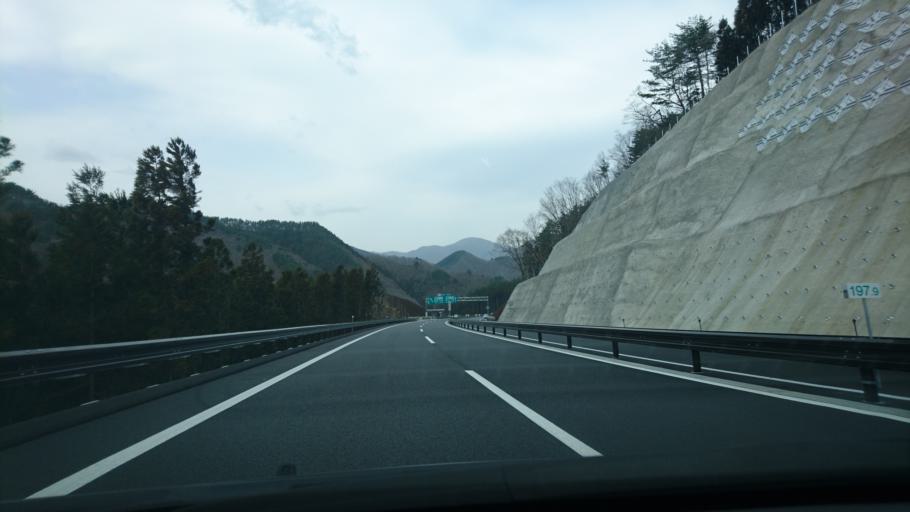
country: JP
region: Iwate
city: Kamaishi
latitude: 39.2473
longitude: 141.8398
